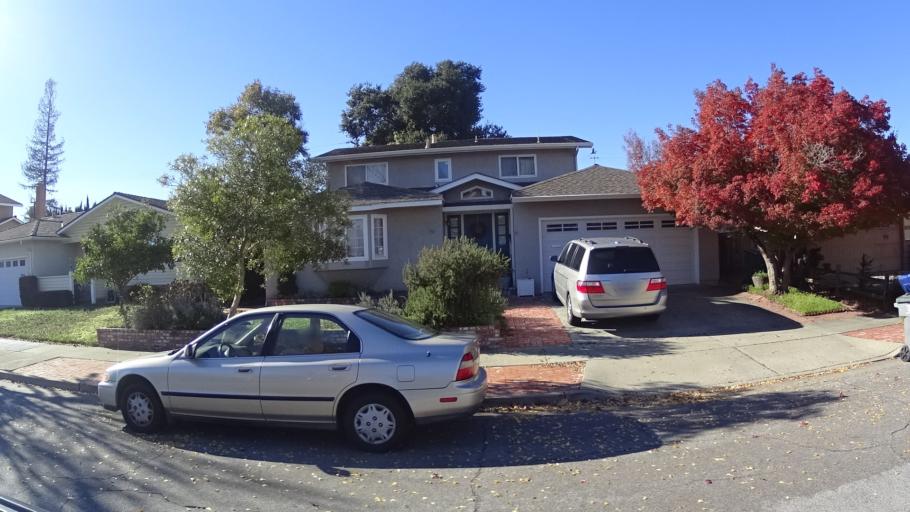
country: US
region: California
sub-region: Santa Clara County
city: Cupertino
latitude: 37.3430
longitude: -122.0189
